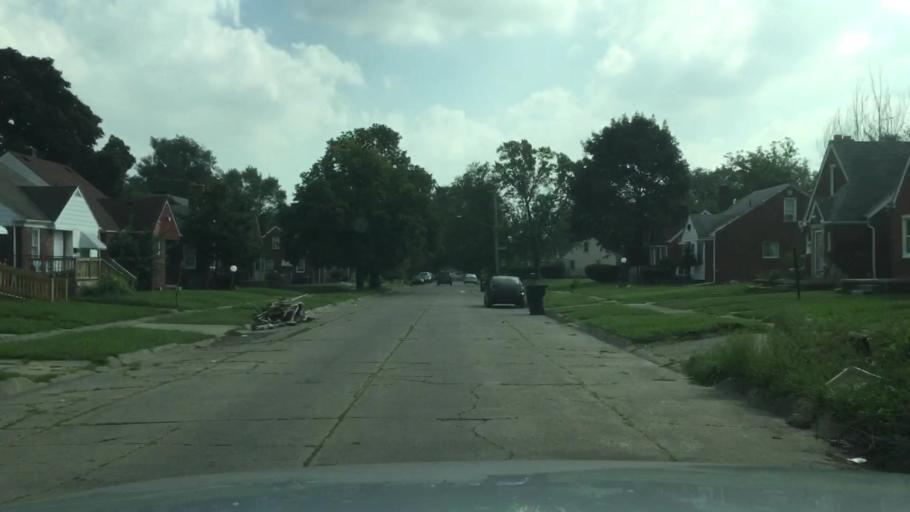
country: US
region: Michigan
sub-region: Wayne County
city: Dearborn
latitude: 42.3567
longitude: -83.1937
